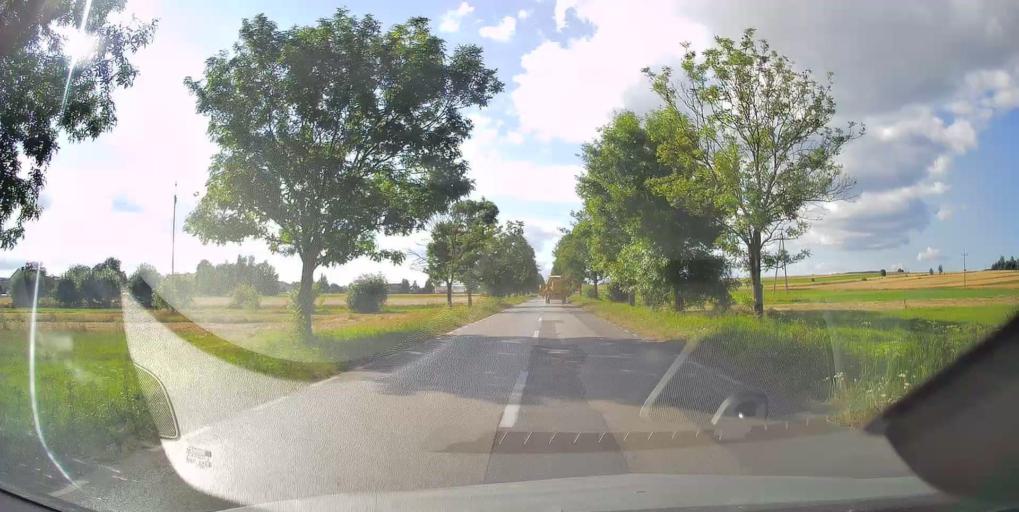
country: PL
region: Swietokrzyskie
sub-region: Powiat kielecki
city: Bodzentyn
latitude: 50.9622
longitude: 20.9009
